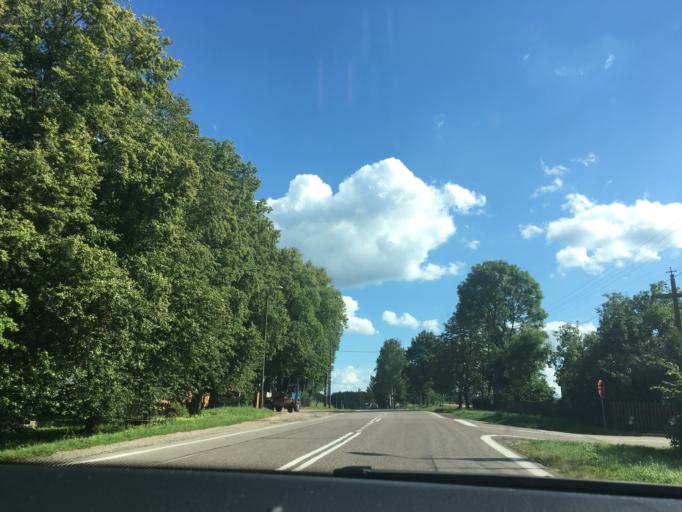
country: PL
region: Podlasie
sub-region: Powiat bialostocki
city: Dobrzyniewo Duze
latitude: 53.3456
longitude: 23.0987
